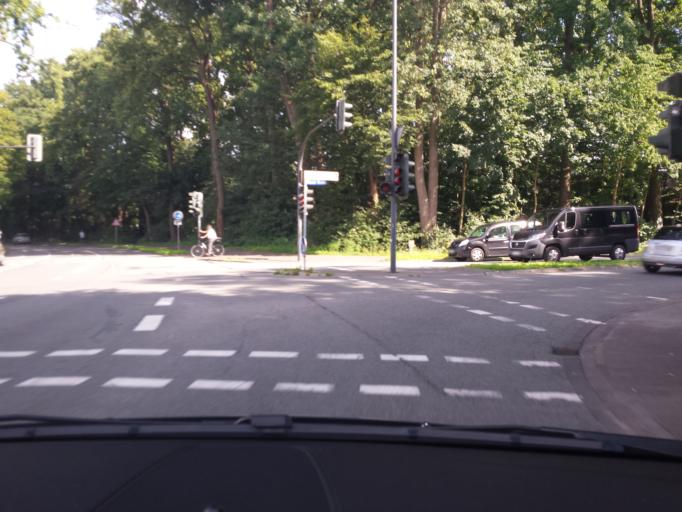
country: DE
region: North Rhine-Westphalia
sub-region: Regierungsbezirk Arnsberg
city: Lippstadt
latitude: 51.6773
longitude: 8.3279
